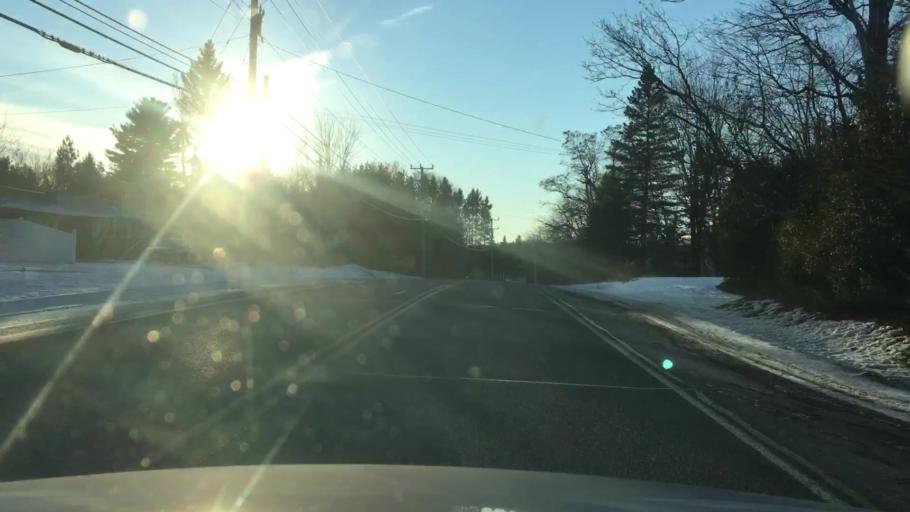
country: US
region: Maine
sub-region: Penobscot County
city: Eddington
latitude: 44.8190
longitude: -68.7017
